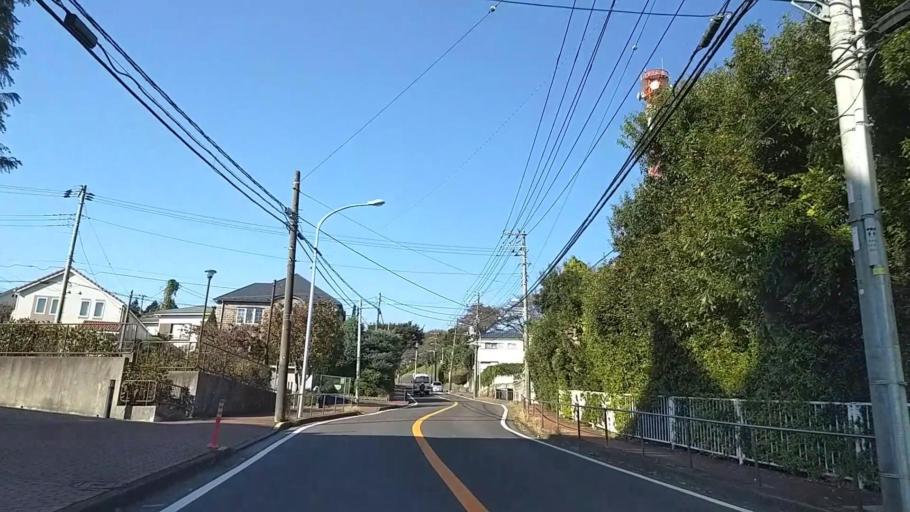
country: JP
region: Kanagawa
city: Yokohama
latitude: 35.4654
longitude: 139.5746
